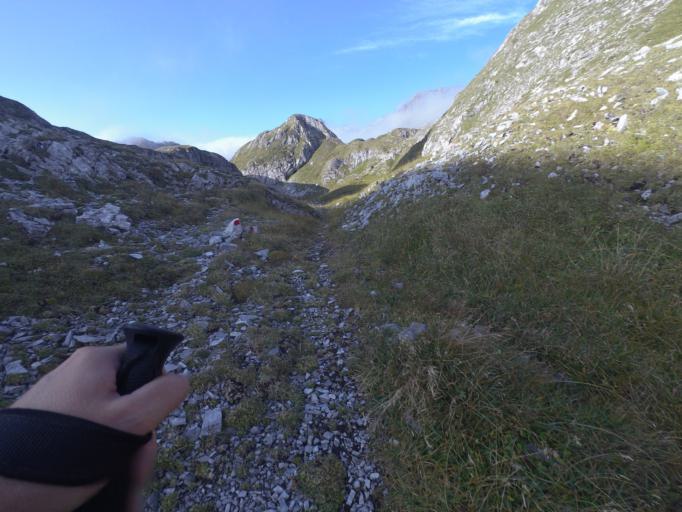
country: AT
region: Salzburg
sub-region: Politischer Bezirk Tamsweg
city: Zederhaus
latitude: 47.2248
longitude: 13.4234
